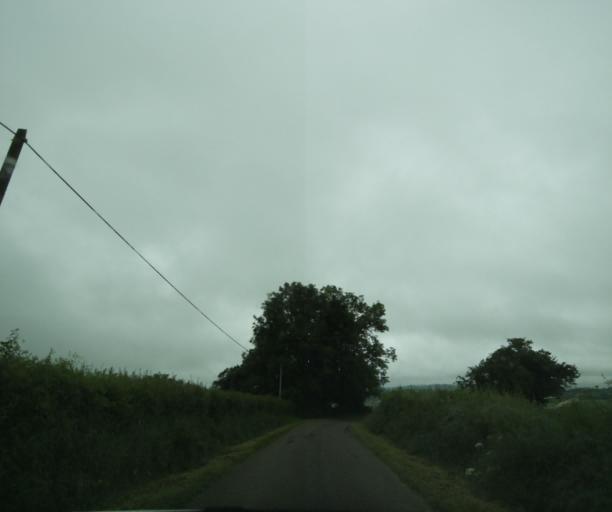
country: FR
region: Bourgogne
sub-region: Departement de Saone-et-Loire
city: Charolles
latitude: 46.3553
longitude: 4.2303
